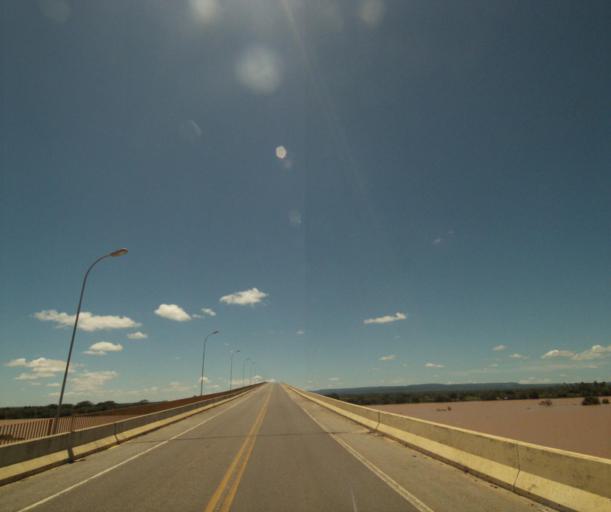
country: BR
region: Bahia
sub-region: Carinhanha
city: Carinhanha
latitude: -14.3237
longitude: -43.7721
